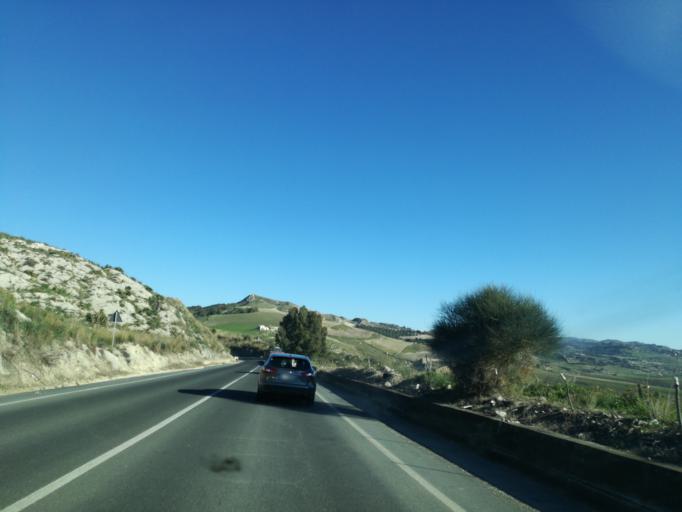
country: IT
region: Sicily
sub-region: Catania
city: San Michele di Ganzaria
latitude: 37.2344
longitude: 14.4492
